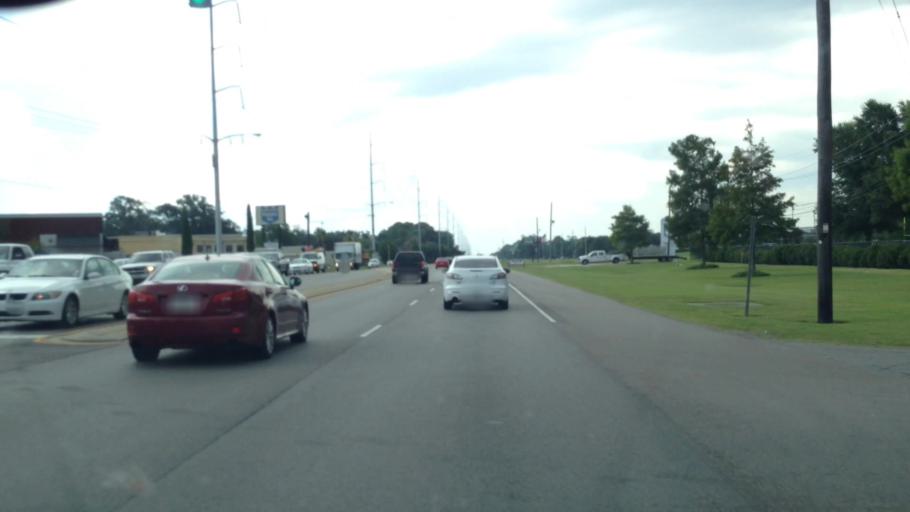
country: US
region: Louisiana
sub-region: Jefferson Parish
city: Elmwood
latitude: 29.9767
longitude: -90.1962
